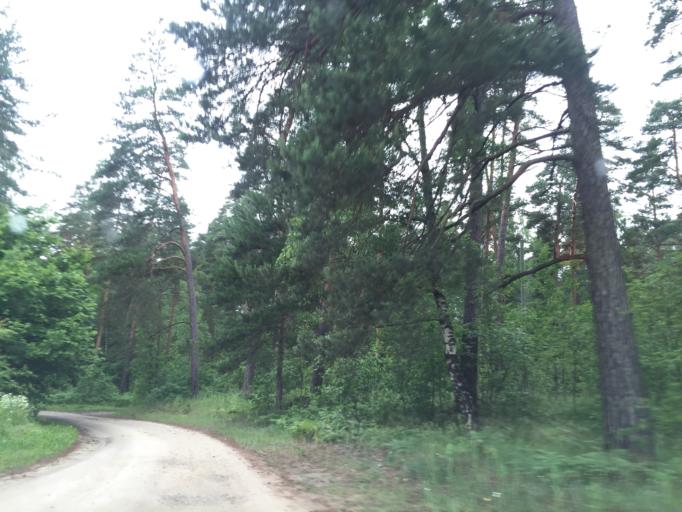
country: LV
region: Riga
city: Jaunciems
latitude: 57.0231
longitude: 24.2158
